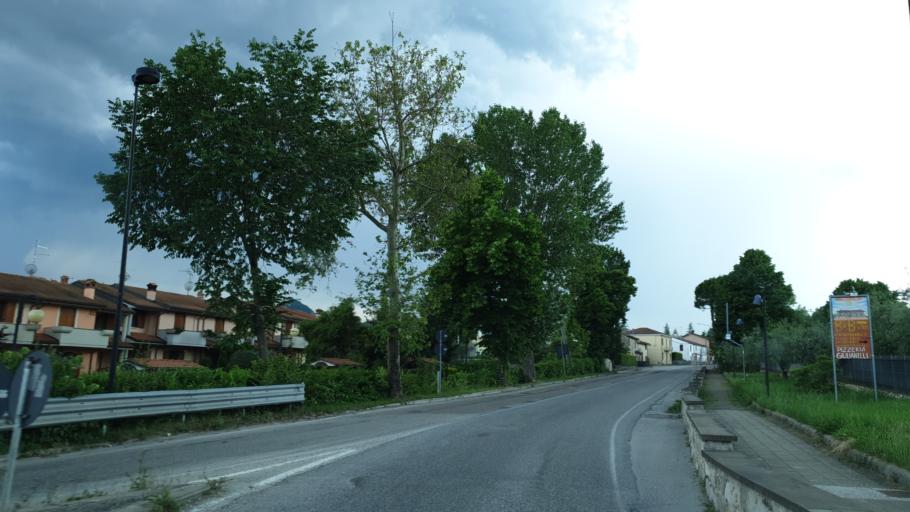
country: IT
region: Emilia-Romagna
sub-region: Provincia di Rimini
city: Secchiano
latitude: 43.9285
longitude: 12.3230
